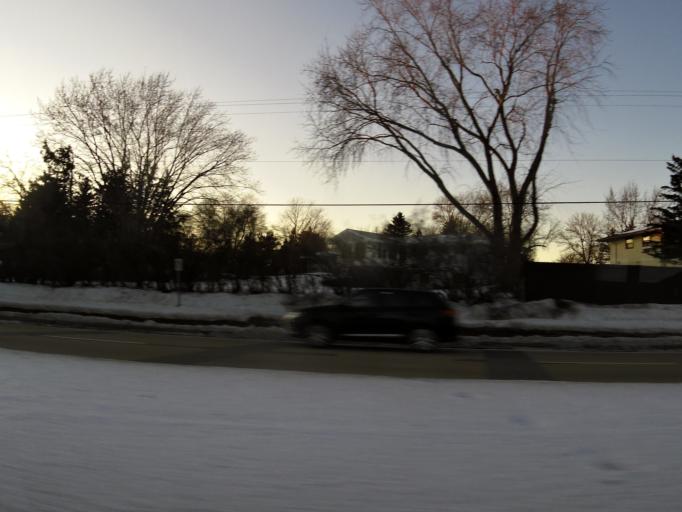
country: US
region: Minnesota
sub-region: Ramsey County
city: North Saint Paul
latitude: 45.0410
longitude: -93.0158
